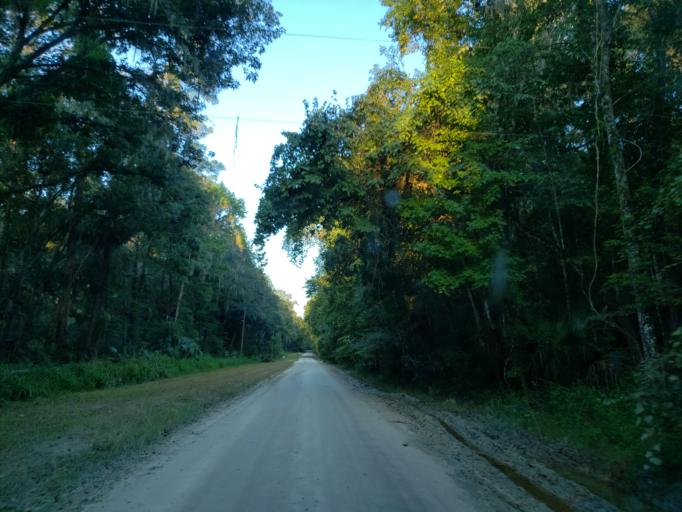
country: US
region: Florida
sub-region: Marion County
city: Citra
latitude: 29.4842
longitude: -82.2676
